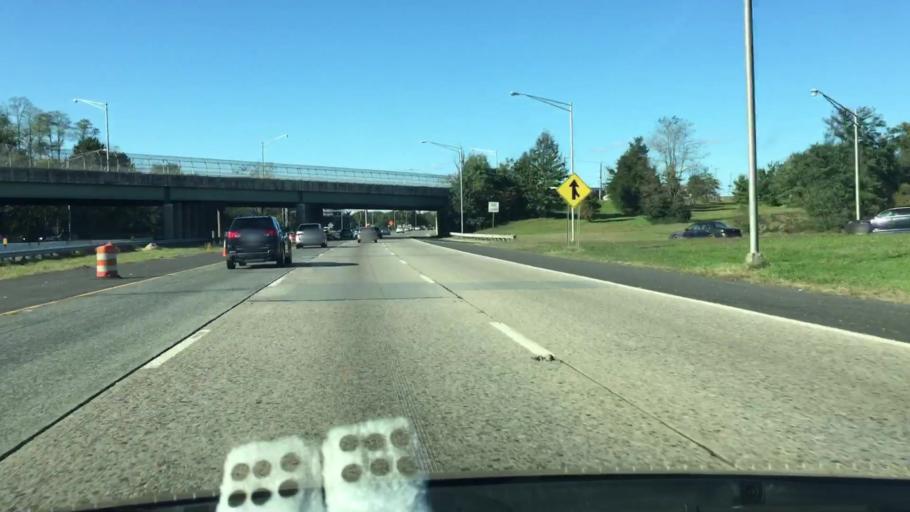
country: US
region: New Jersey
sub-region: Camden County
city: Glendora
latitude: 39.8304
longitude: -75.0881
